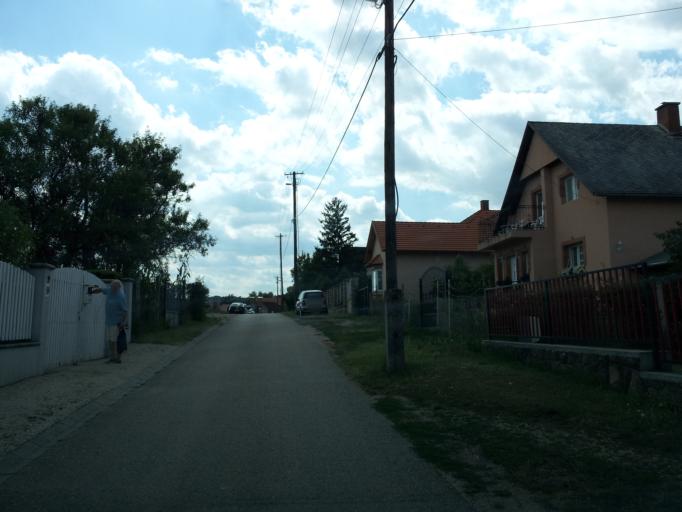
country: HU
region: Veszprem
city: Balatonalmadi
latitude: 47.0477
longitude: 18.0089
